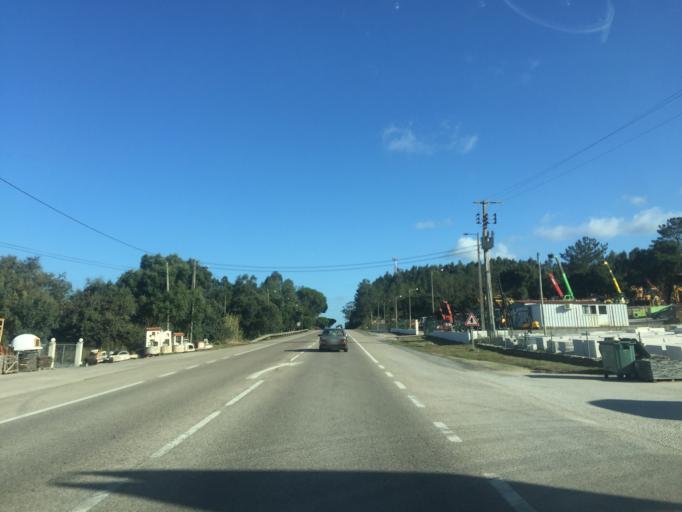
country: PT
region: Leiria
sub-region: Alcobaca
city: Turquel
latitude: 39.4837
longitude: -8.9355
